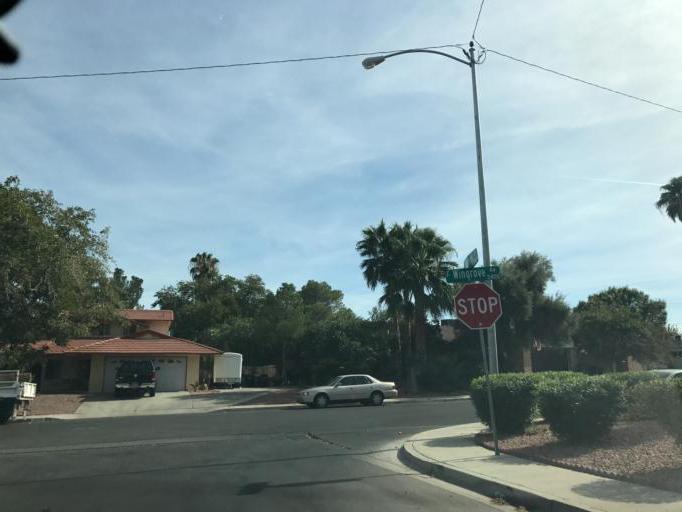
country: US
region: Nevada
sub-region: Clark County
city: Winchester
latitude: 36.1278
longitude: -115.0999
